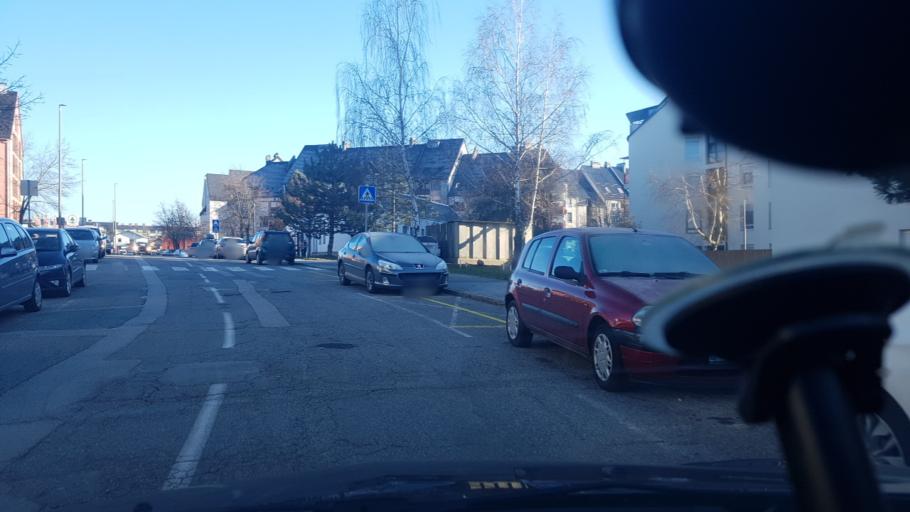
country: SI
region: Ptuj
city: Ptuj
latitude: 46.4296
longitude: 15.8689
